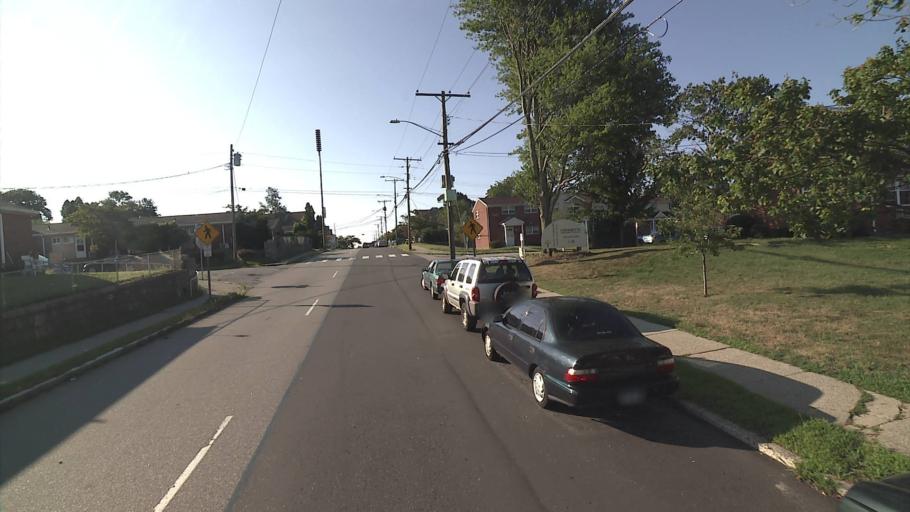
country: US
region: Connecticut
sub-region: New London County
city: New London
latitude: 41.3521
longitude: -72.1127
